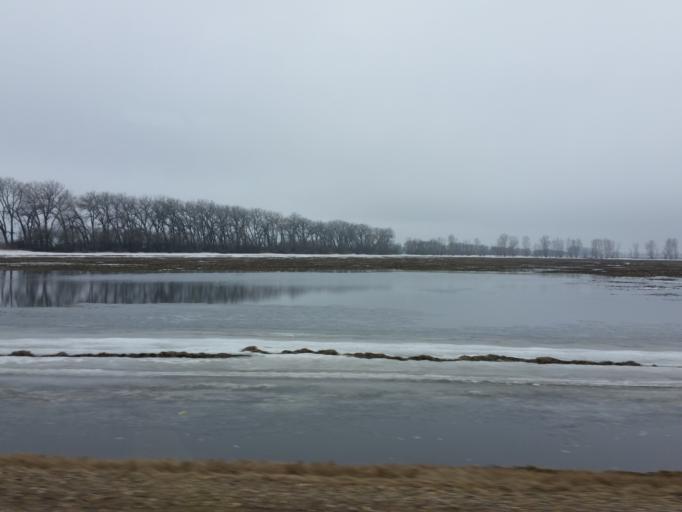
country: US
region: North Dakota
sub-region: Walsh County
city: Grafton
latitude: 48.6103
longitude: -97.4487
